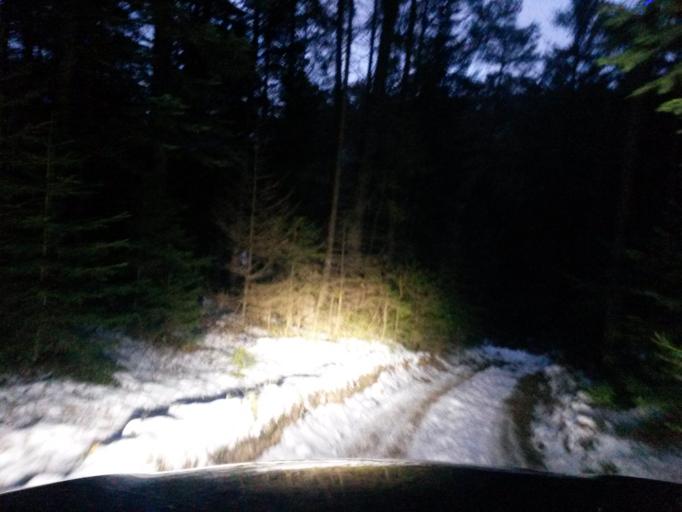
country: SK
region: Kosicky
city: Medzev
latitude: 48.7863
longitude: 20.8030
